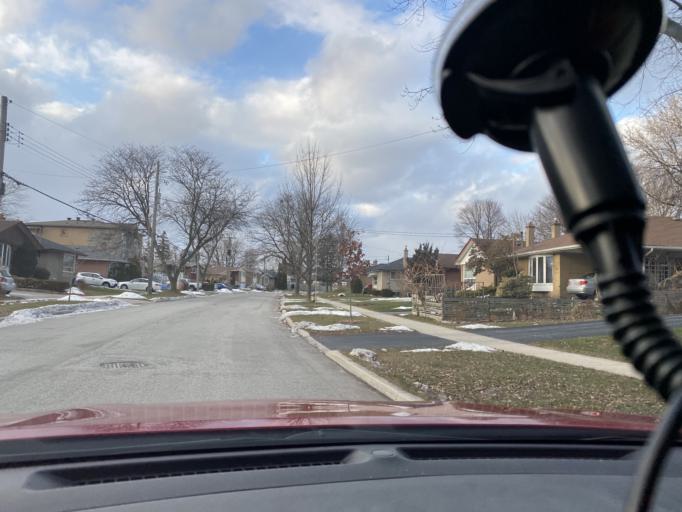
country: CA
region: Ontario
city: Scarborough
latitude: 43.7689
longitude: -79.2161
